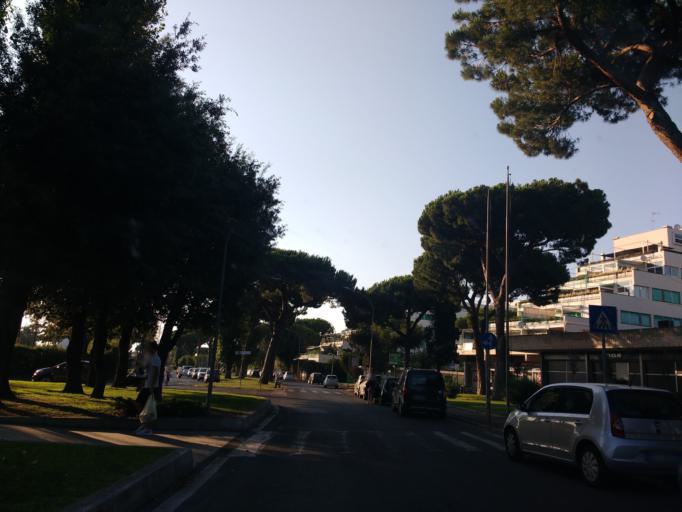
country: IT
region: Latium
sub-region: Citta metropolitana di Roma Capitale
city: Acilia-Castel Fusano-Ostia Antica
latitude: 41.7497
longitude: 12.3531
